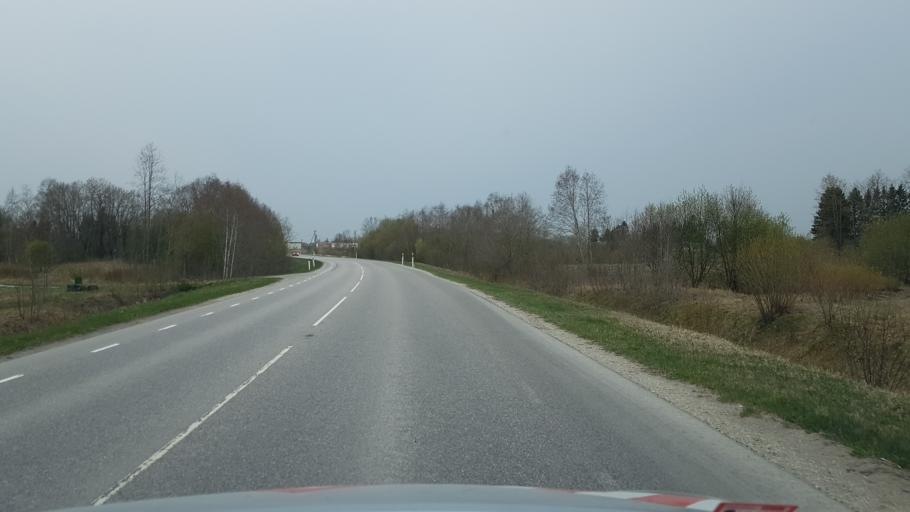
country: EE
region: Harju
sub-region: Joelaehtme vald
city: Loo
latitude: 59.4112
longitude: 24.9272
